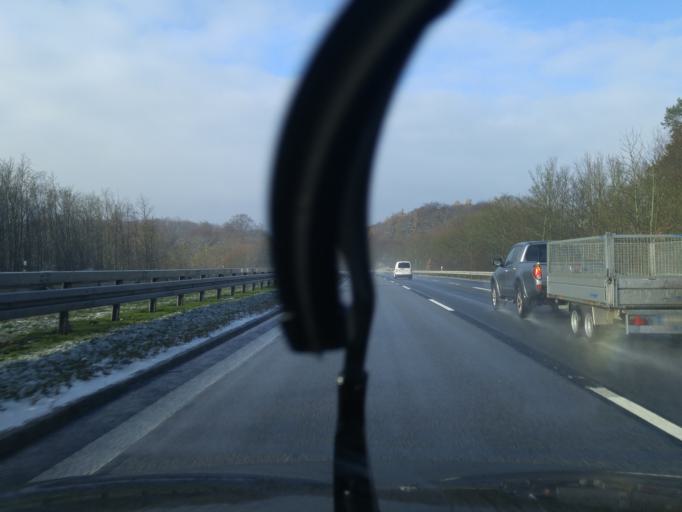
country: DE
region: Bavaria
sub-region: Regierungsbezirk Unterfranken
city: Wasserlosen
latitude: 50.0779
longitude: 10.0094
